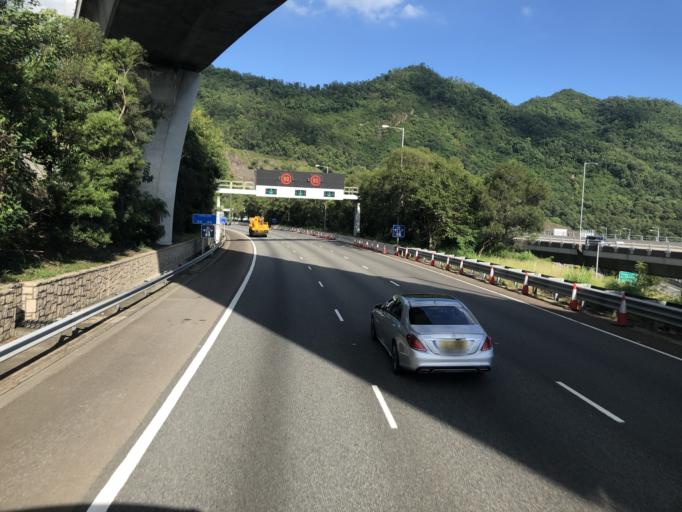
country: HK
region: Tsuen Wan
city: Tsuen Wan
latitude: 22.3454
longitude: 114.0917
